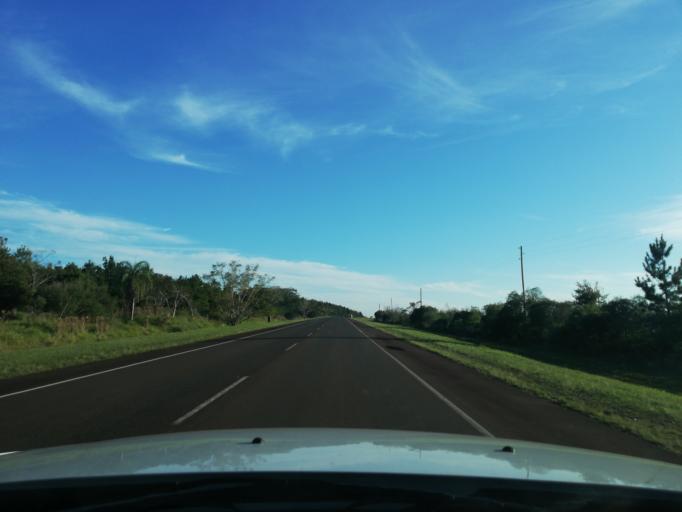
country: AR
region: Misiones
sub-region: Departamento de Capital
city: Posadas
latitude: -27.4338
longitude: -56.0112
